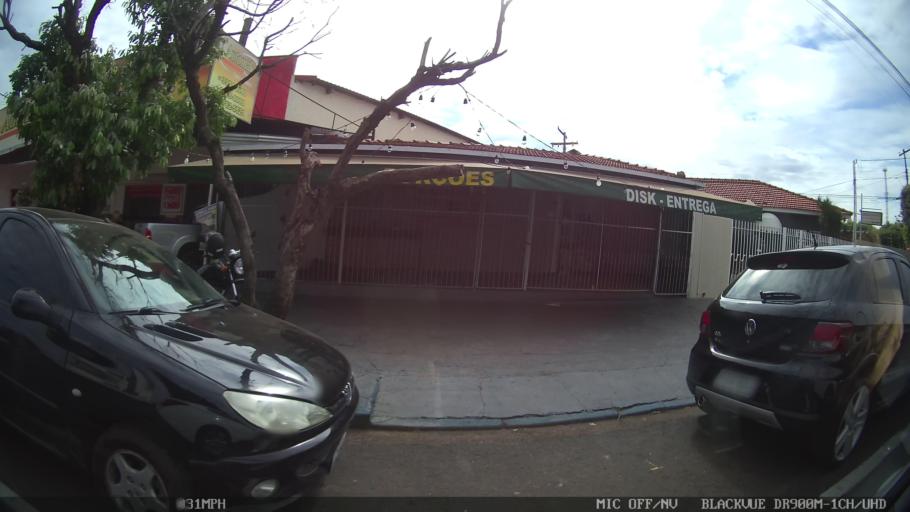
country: BR
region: Sao Paulo
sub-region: Sao Jose Do Rio Preto
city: Sao Jose do Rio Preto
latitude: -20.8171
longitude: -49.3604
